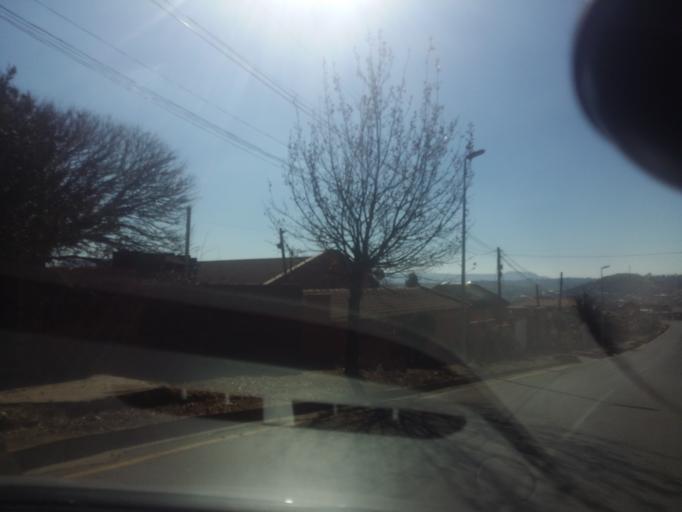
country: LS
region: Maseru
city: Maseru
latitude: -29.3421
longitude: 27.4483
